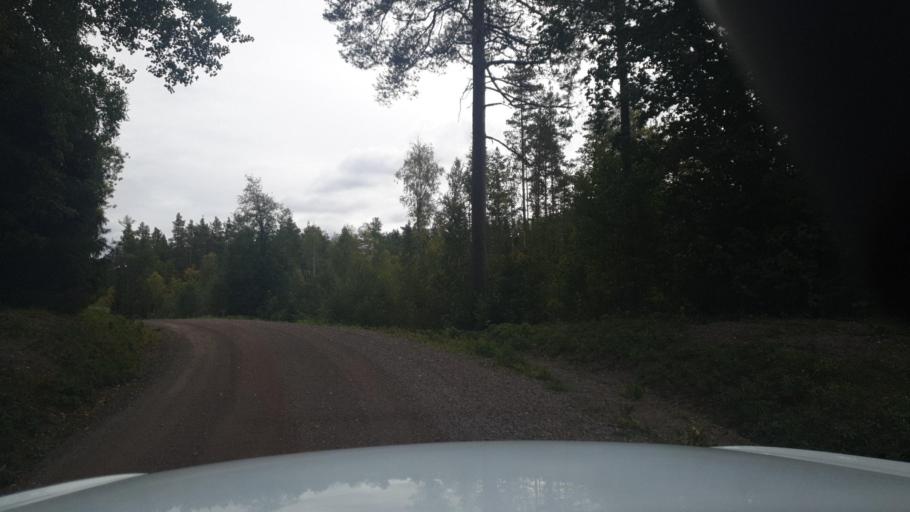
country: SE
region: Vaermland
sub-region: Eda Kommun
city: Charlottenberg
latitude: 60.0903
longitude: 12.5042
